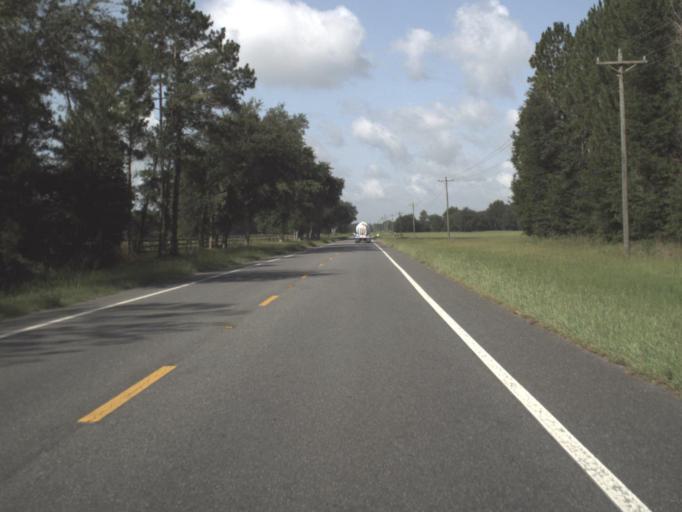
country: US
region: Florida
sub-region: Columbia County
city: Lake City
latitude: 30.1074
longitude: -82.7394
